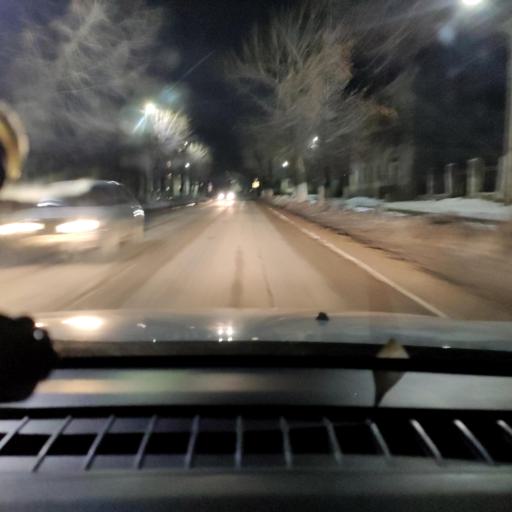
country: RU
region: Samara
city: Novokuybyshevsk
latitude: 53.0960
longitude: 49.9461
